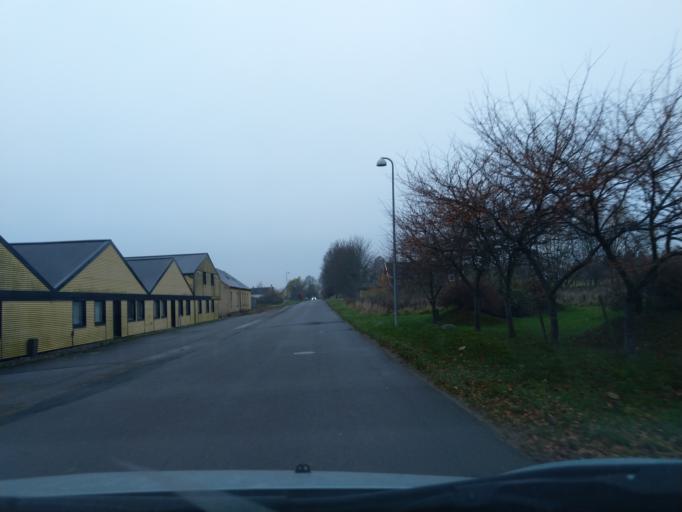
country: DK
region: Zealand
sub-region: Vordingborg Kommune
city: Praesto
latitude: 55.1075
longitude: 12.0748
